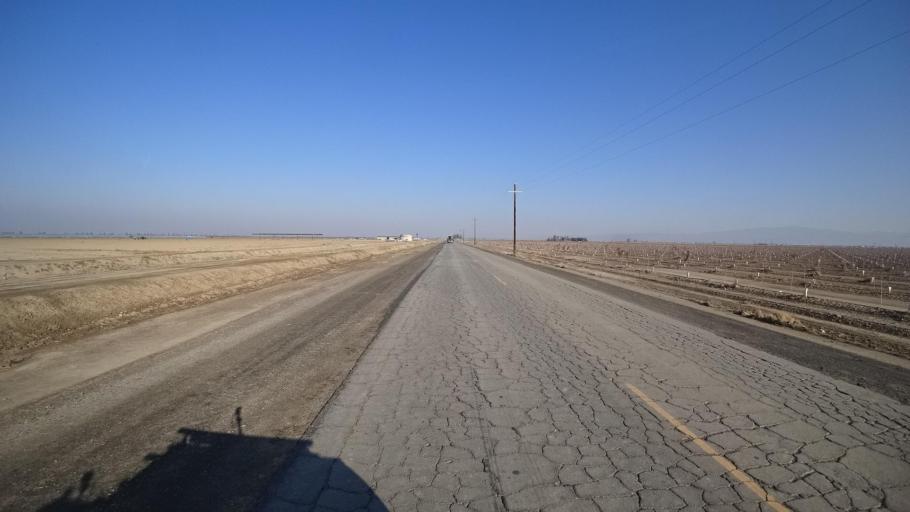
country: US
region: California
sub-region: Kern County
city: Weedpatch
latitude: 35.1876
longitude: -118.9678
